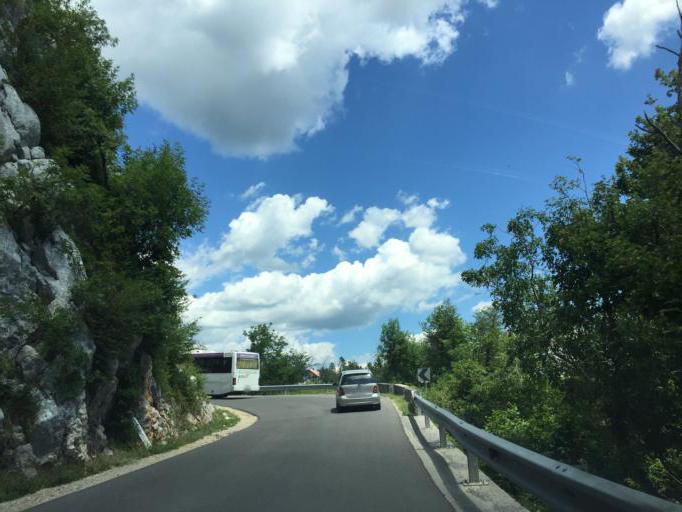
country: SI
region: Postojna
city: Postojna
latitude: 45.8183
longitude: 14.1362
